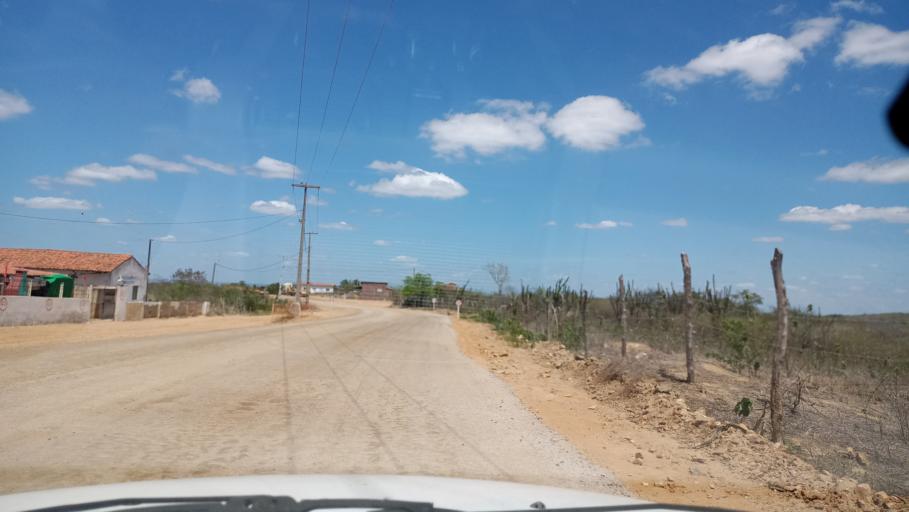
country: BR
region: Rio Grande do Norte
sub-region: Sao Paulo Do Potengi
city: Sao Paulo do Potengi
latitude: -5.7787
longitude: -35.9143
